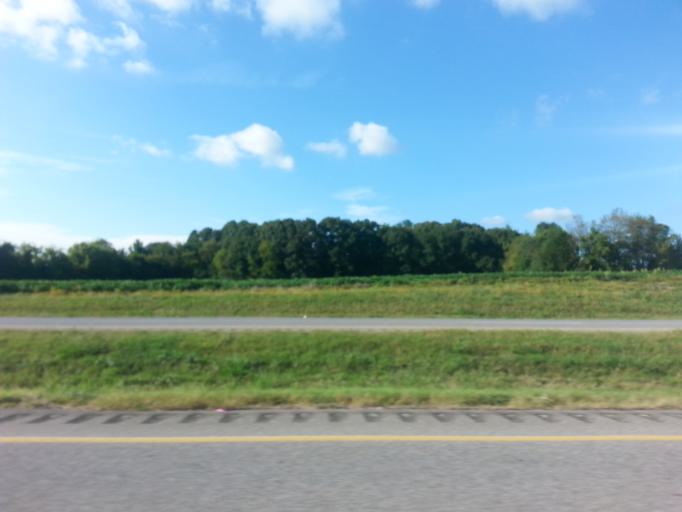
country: US
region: Alabama
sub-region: Colbert County
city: Tuscumbia
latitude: 34.7096
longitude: -87.7359
